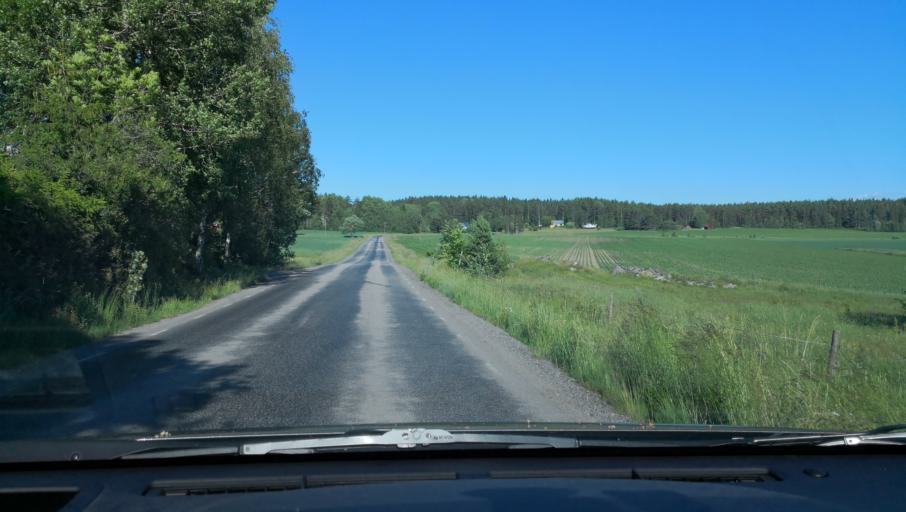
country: SE
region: Soedermanland
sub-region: Eskilstuna Kommun
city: Arla
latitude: 59.3264
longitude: 16.6594
